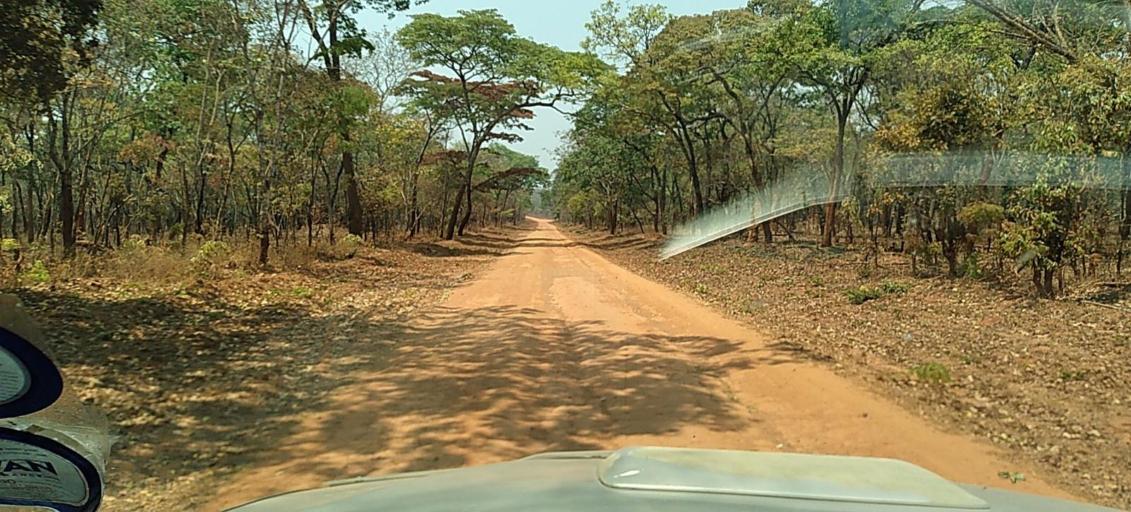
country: ZM
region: North-Western
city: Kasempa
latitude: -13.5602
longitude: 26.0813
